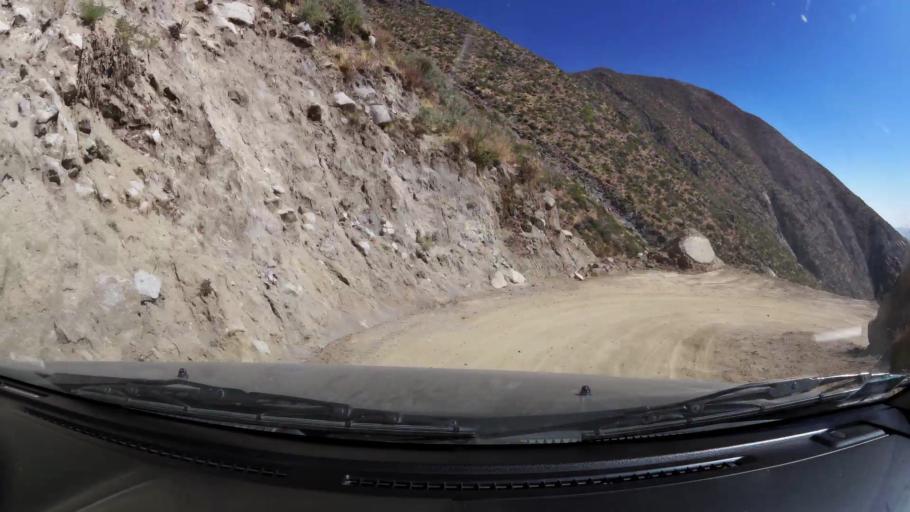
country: PE
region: Huancavelica
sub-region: Huaytara
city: Quito-Arma
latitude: -13.6200
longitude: -75.3537
